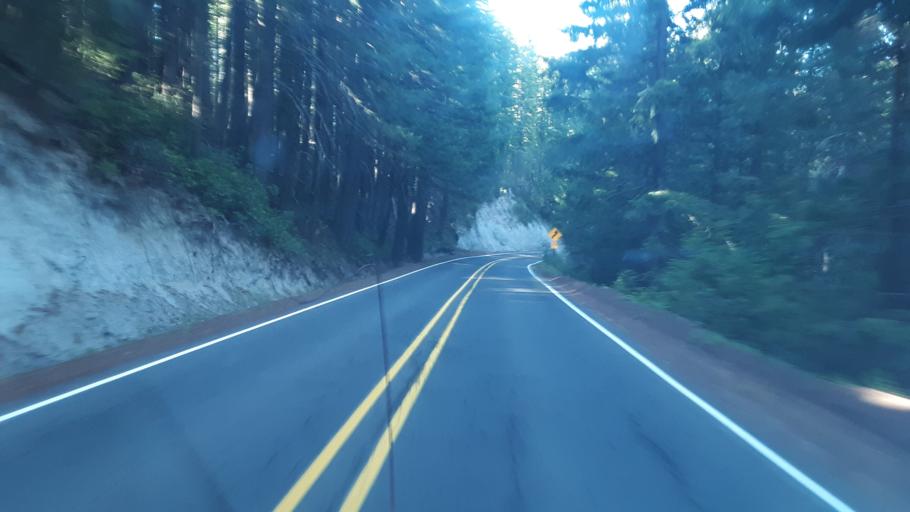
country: US
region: Oregon
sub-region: Jackson County
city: Shady Cove
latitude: 42.9376
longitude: -122.4198
